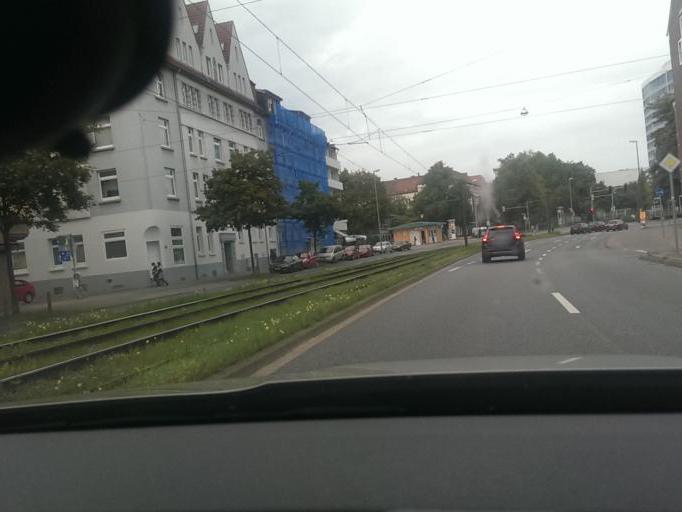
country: DE
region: Lower Saxony
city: Hannover
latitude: 52.3605
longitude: 9.7216
